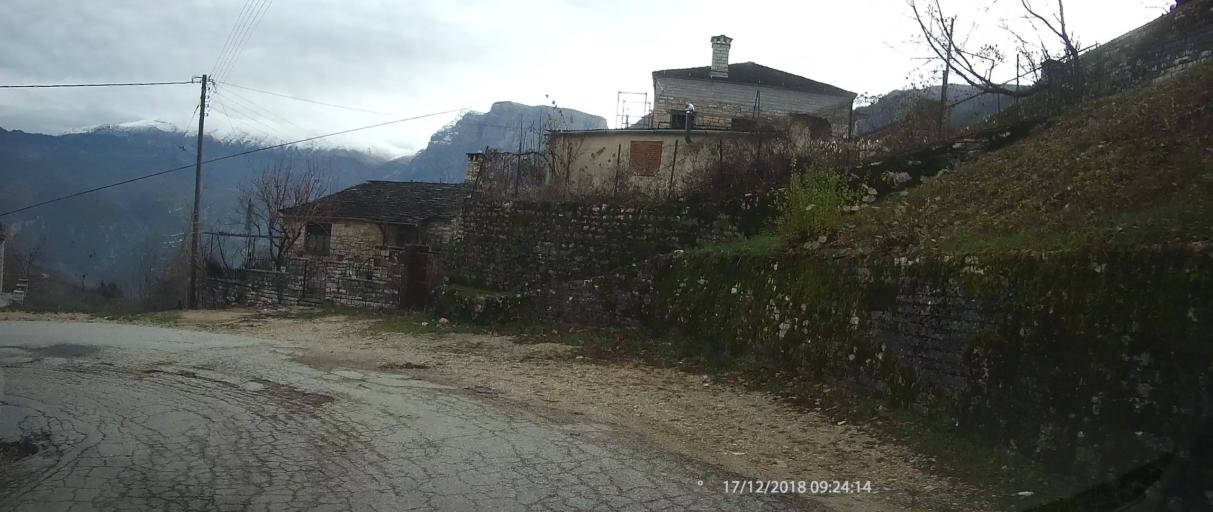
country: GR
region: Epirus
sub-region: Nomos Ioanninon
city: Kalpaki
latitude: 39.9340
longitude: 20.6721
